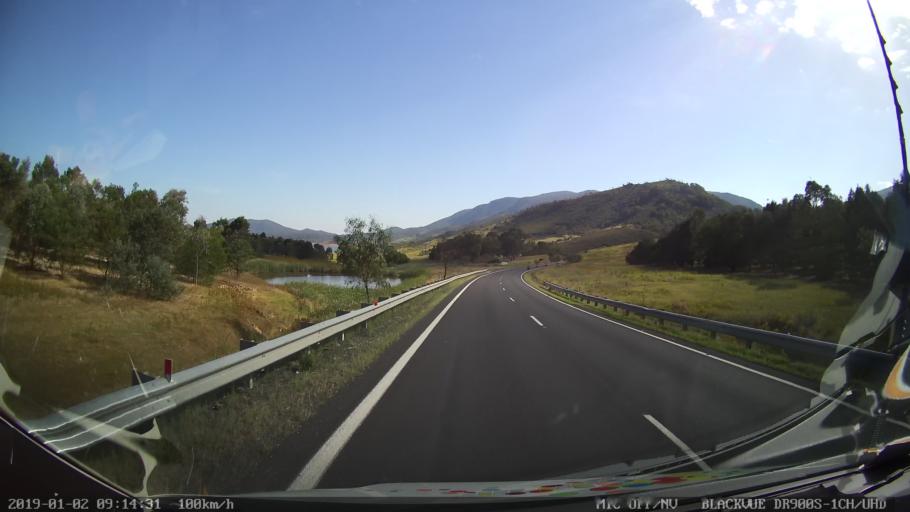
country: AU
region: New South Wales
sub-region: Tumut Shire
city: Tumut
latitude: -35.4763
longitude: 148.2745
